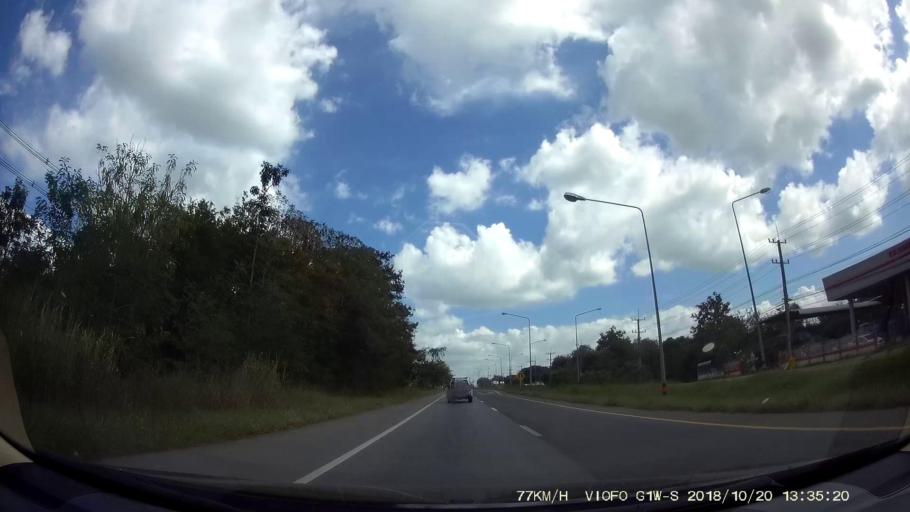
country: TH
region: Khon Kaen
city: Chum Phae
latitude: 16.5690
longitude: 102.0455
